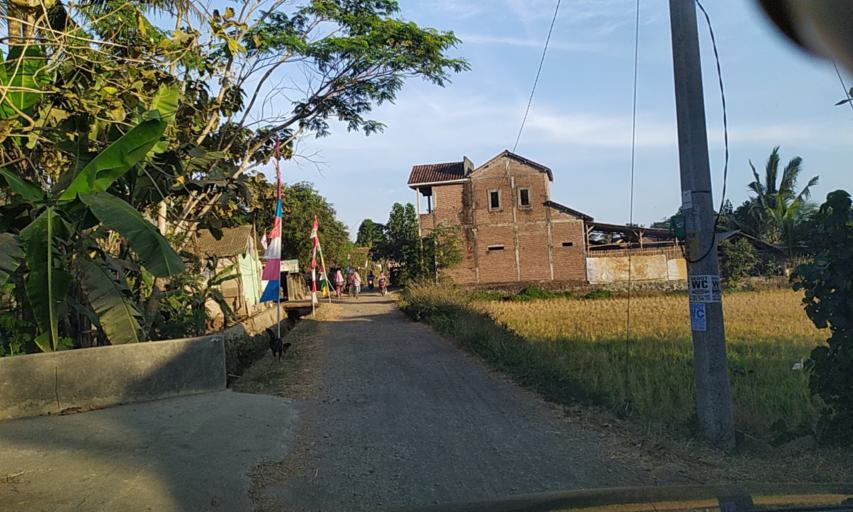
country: ID
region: Central Java
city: Rejanegara
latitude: -7.6921
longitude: 109.0440
